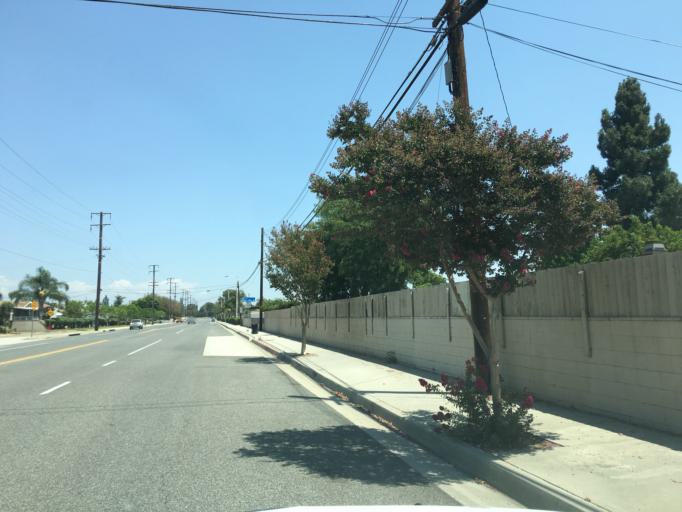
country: US
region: California
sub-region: Los Angeles County
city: Charter Oak
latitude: 34.0994
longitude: -117.8432
